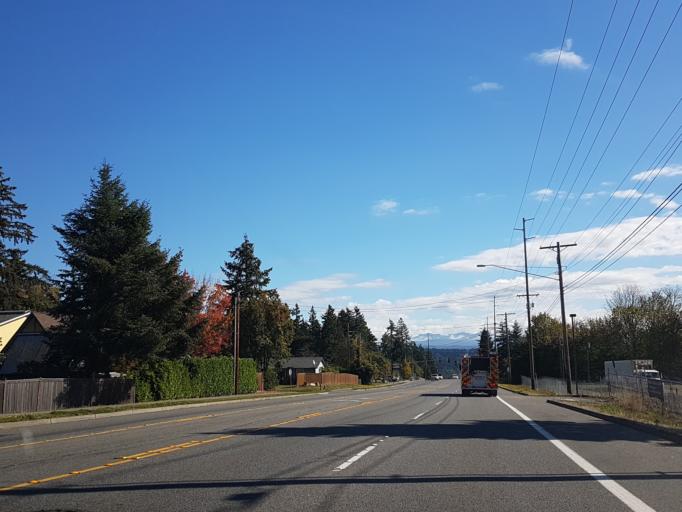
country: US
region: Washington
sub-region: King County
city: Kenmore
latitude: 47.7913
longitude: -122.2360
